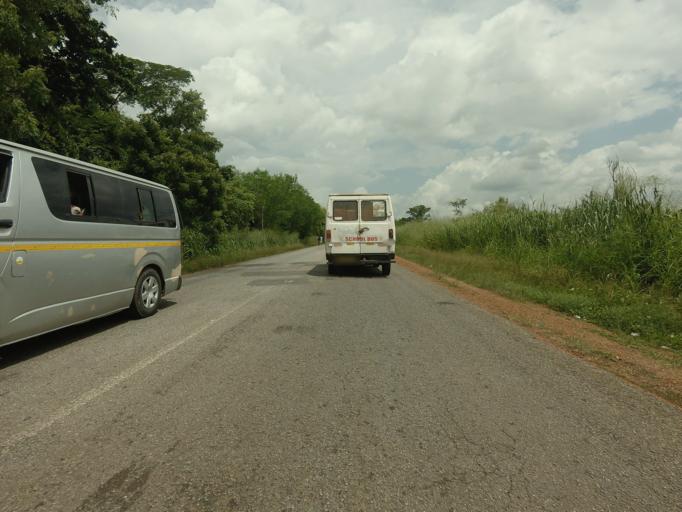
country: GH
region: Volta
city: Ho
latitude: 6.3268
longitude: 0.1640
